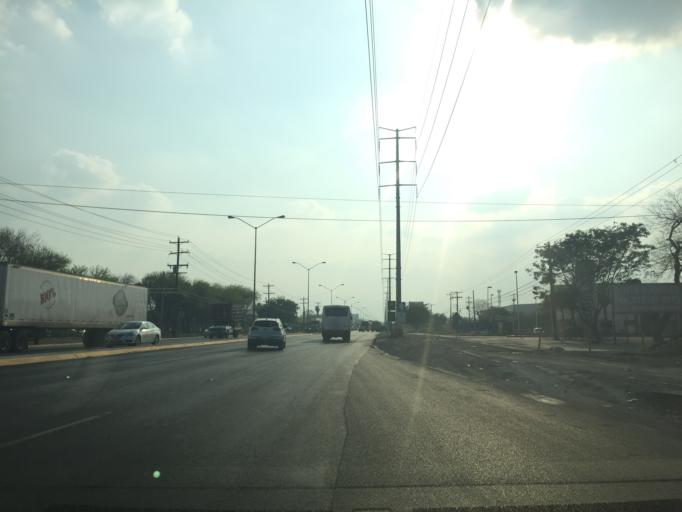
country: MX
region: Nuevo Leon
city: Apodaca
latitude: 25.7657
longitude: -100.2019
